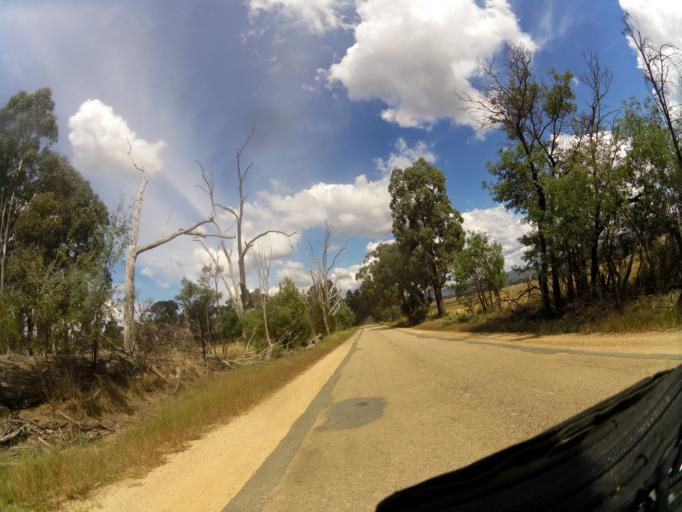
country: AU
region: Victoria
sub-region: Benalla
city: Benalla
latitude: -36.7634
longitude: 145.9766
